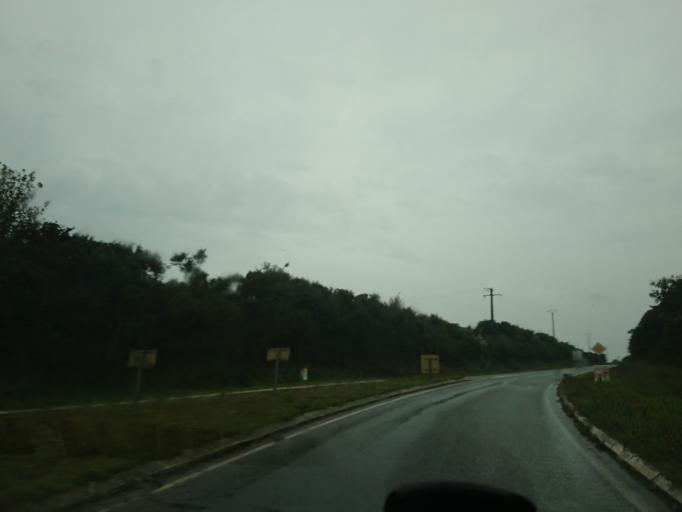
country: FR
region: Brittany
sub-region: Departement du Finistere
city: Plouguerneau
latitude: 48.6036
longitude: -4.5017
